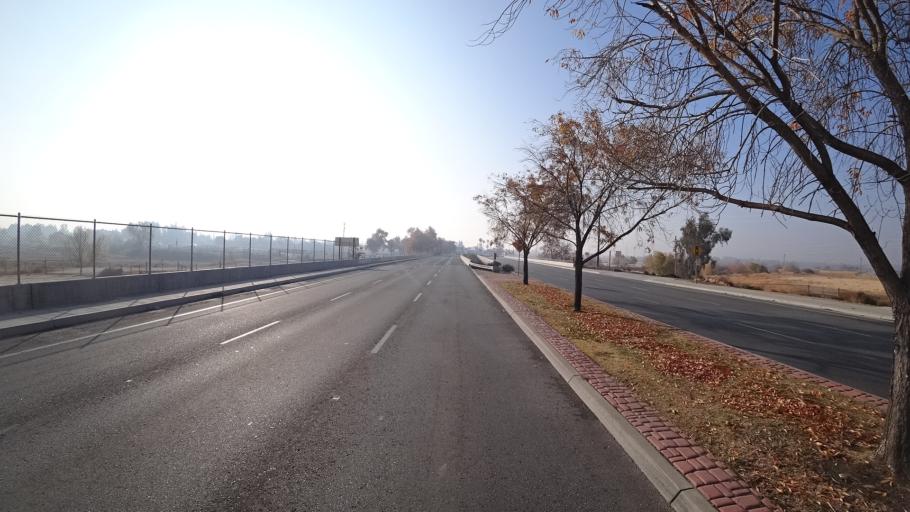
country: US
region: California
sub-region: Kern County
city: Greenacres
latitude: 35.3645
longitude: -119.0918
